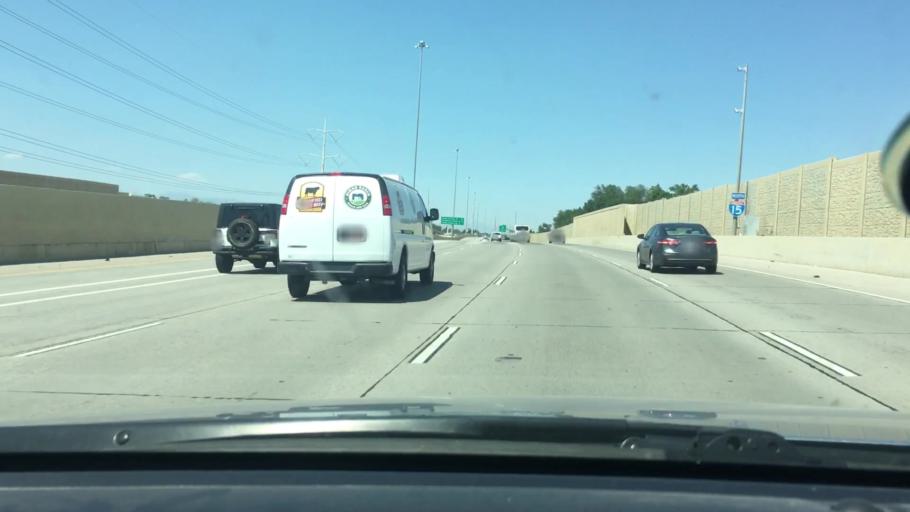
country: US
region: Utah
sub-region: Utah County
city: Provo
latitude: 40.2174
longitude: -111.6666
